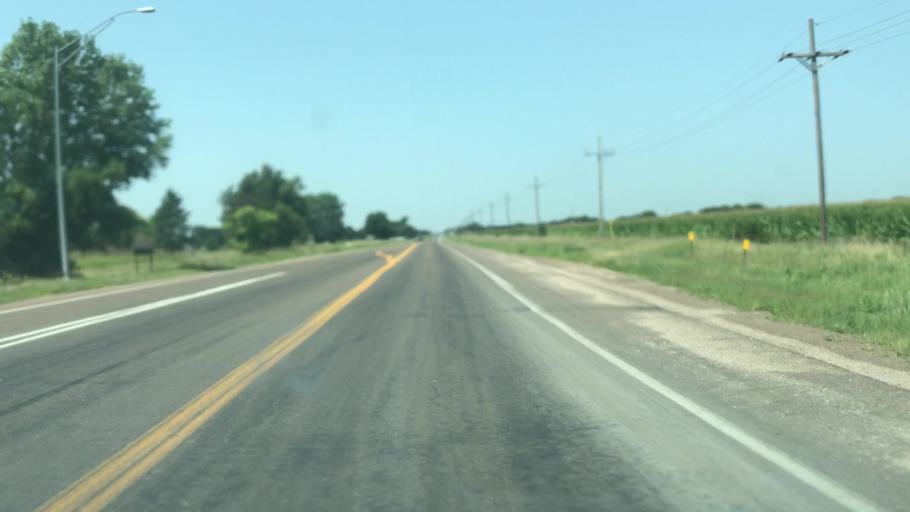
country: US
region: Nebraska
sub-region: Hall County
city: Grand Island
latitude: 40.8869
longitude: -98.3213
